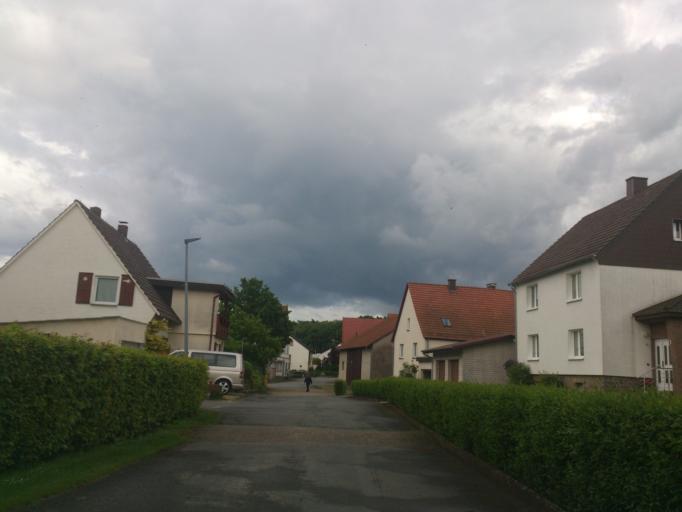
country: DE
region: North Rhine-Westphalia
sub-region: Regierungsbezirk Detmold
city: Willebadessen
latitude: 51.5806
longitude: 9.0362
